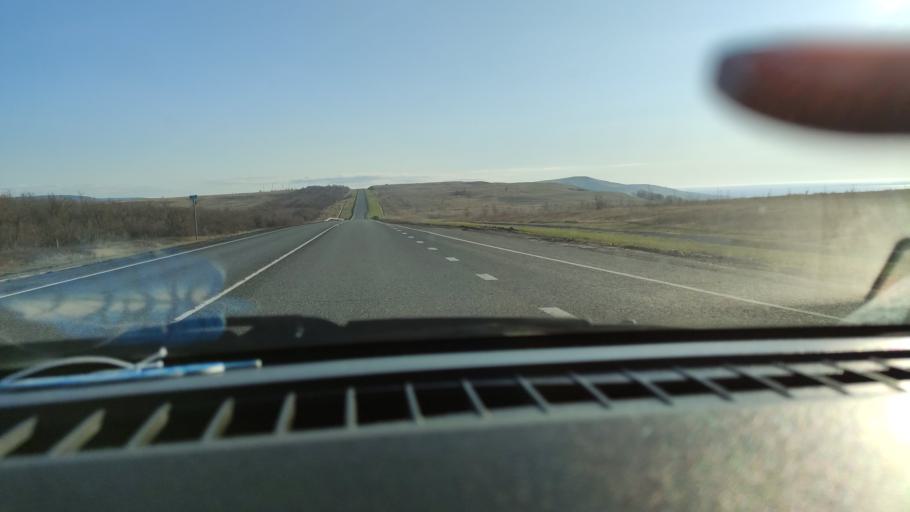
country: RU
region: Saratov
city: Alekseyevka
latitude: 52.2098
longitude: 47.8798
